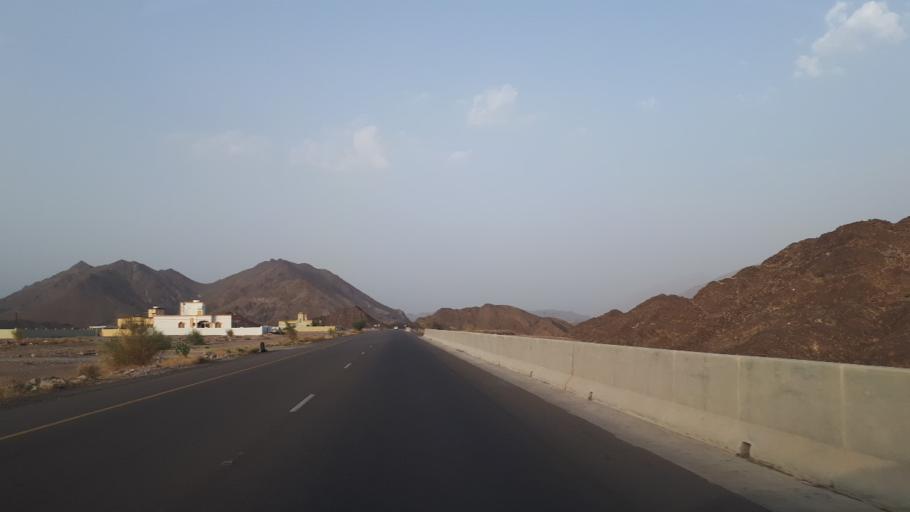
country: OM
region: Al Batinah
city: Rustaq
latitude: 23.3891
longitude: 57.2030
